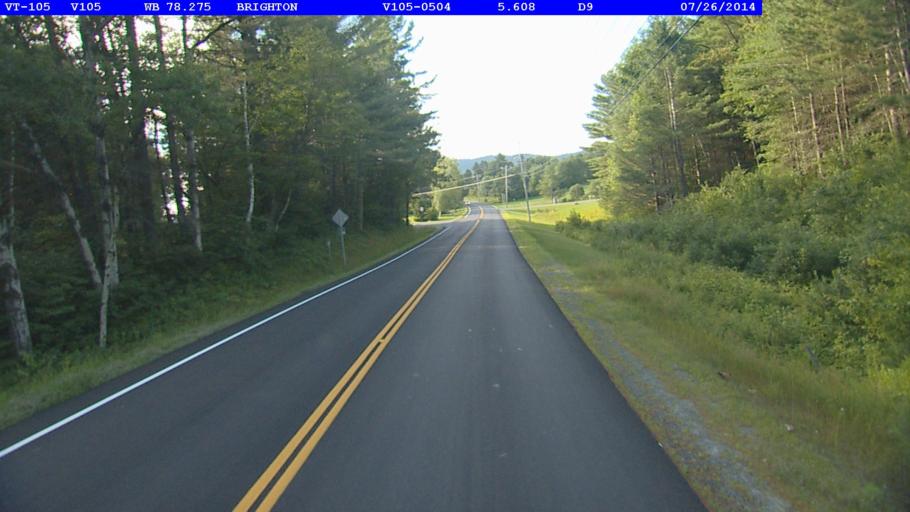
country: US
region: Vermont
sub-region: Caledonia County
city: Lyndonville
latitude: 44.8109
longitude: -71.8616
